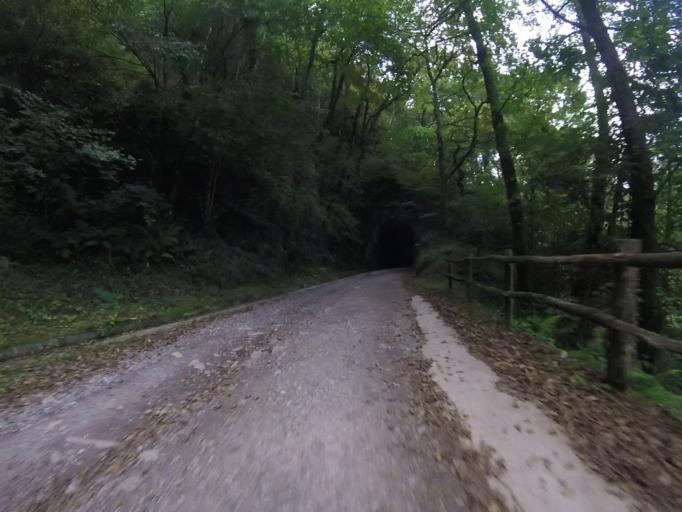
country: ES
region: Basque Country
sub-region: Provincia de Guipuzcoa
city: Andoain
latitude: 43.1919
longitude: -2.0054
